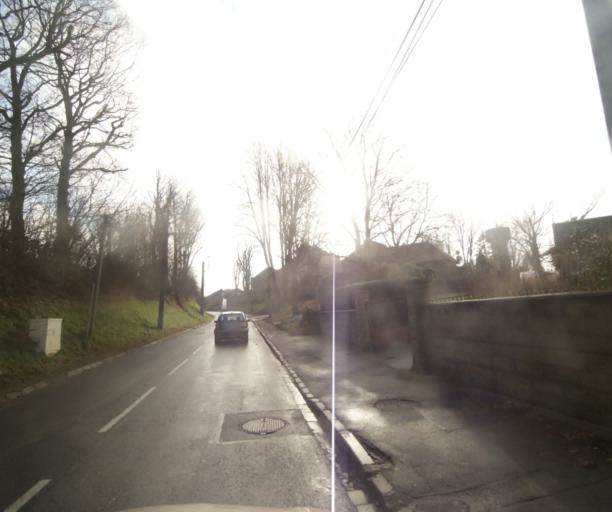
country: FR
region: Nord-Pas-de-Calais
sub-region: Departement du Nord
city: Artres
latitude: 50.2895
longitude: 3.5420
